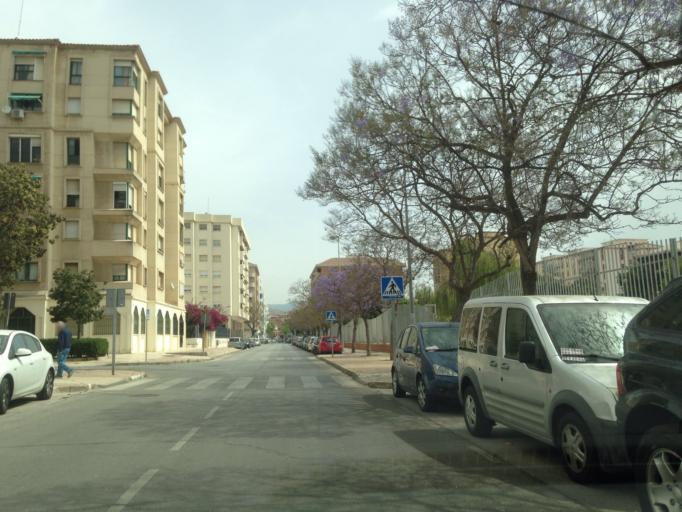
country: ES
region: Andalusia
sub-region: Provincia de Malaga
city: Malaga
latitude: 36.7065
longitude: -4.4337
